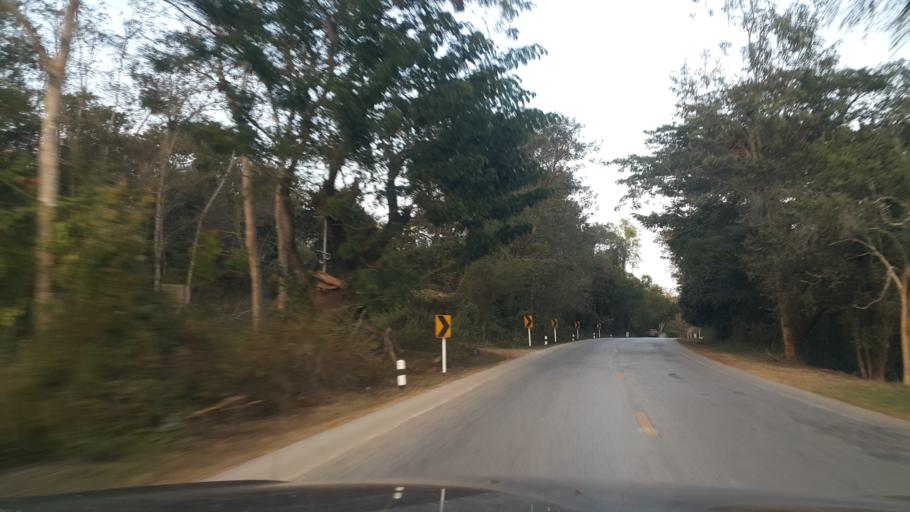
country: TH
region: Loei
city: Loei
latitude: 17.4726
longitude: 101.5979
